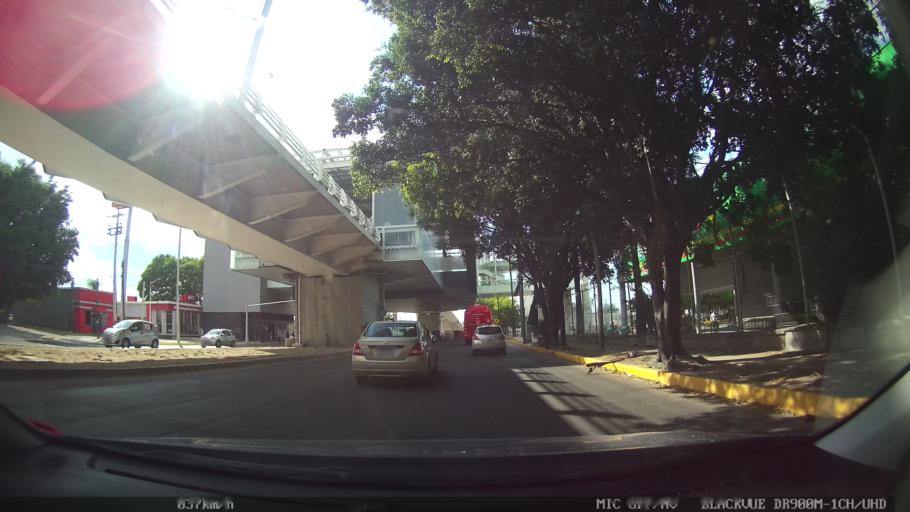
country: MX
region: Jalisco
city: Tlaquepaque
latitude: 20.6308
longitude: -103.2950
